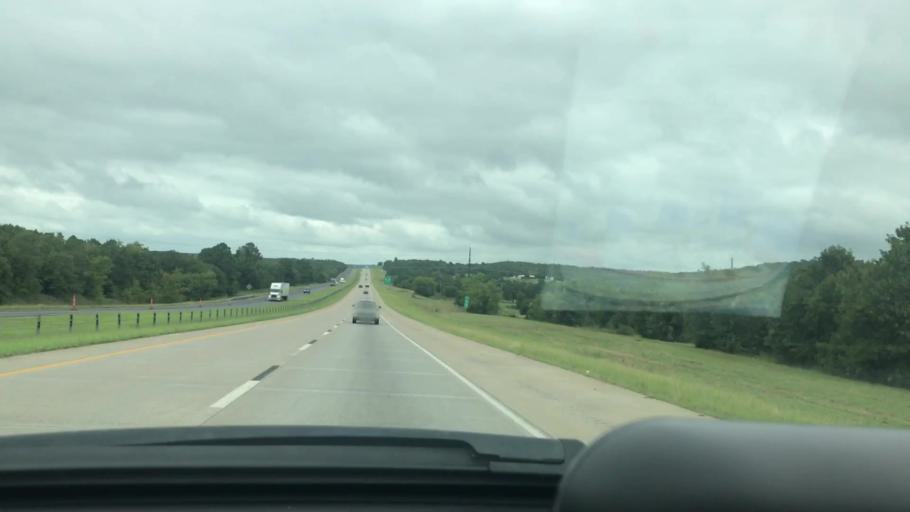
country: US
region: Oklahoma
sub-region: Pittsburg County
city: Krebs
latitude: 34.9744
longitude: -95.7233
